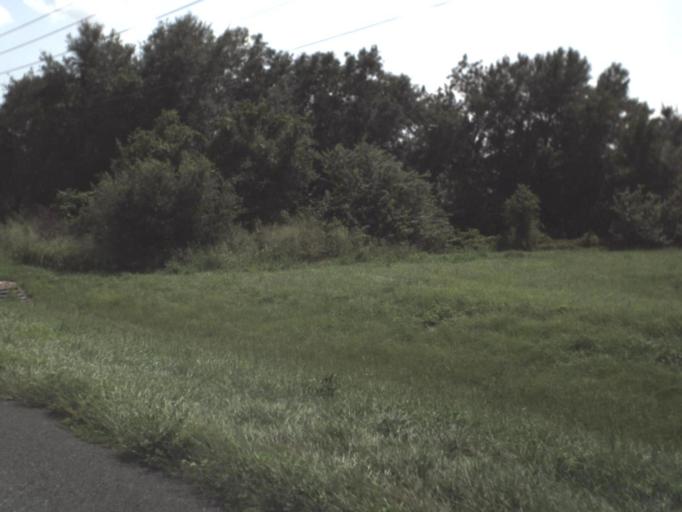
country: US
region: Florida
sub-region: Polk County
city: Lake Hamilton
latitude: 28.0598
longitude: -81.6370
